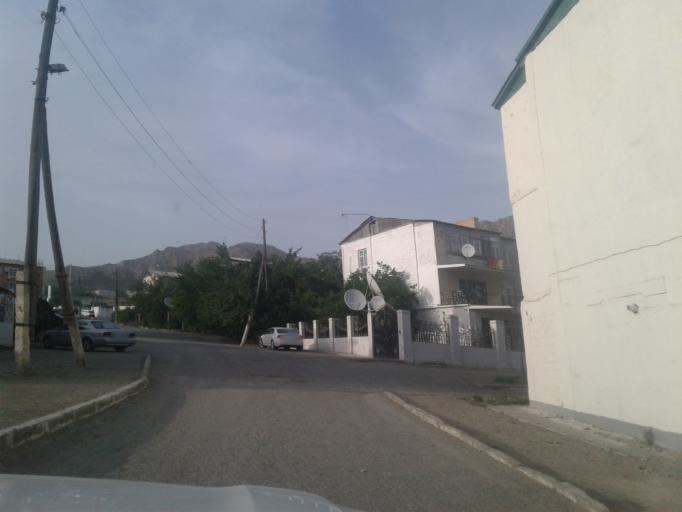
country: TM
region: Balkan
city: Turkmenbasy
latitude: 40.0020
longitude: 52.9640
